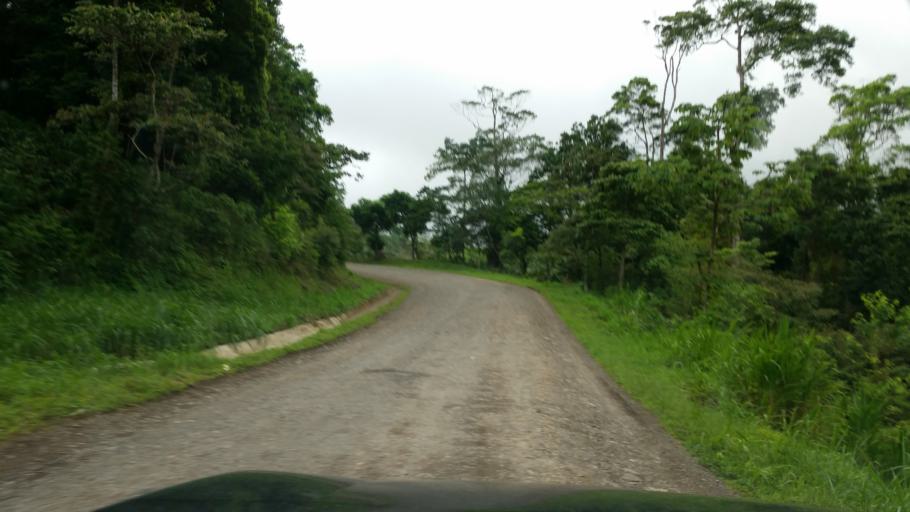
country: NI
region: Jinotega
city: San Jose de Bocay
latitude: 13.2773
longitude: -85.7256
